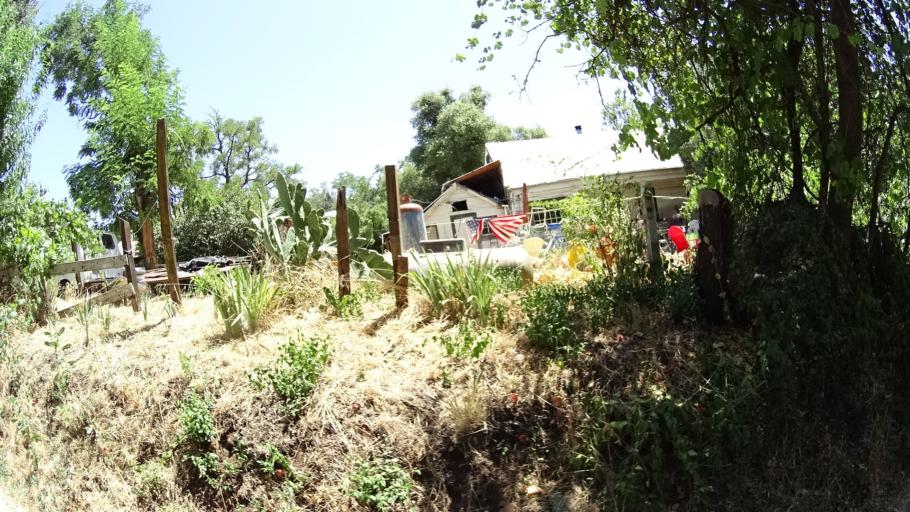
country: US
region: California
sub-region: Amador County
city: Jackson
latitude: 38.3022
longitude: -120.7028
